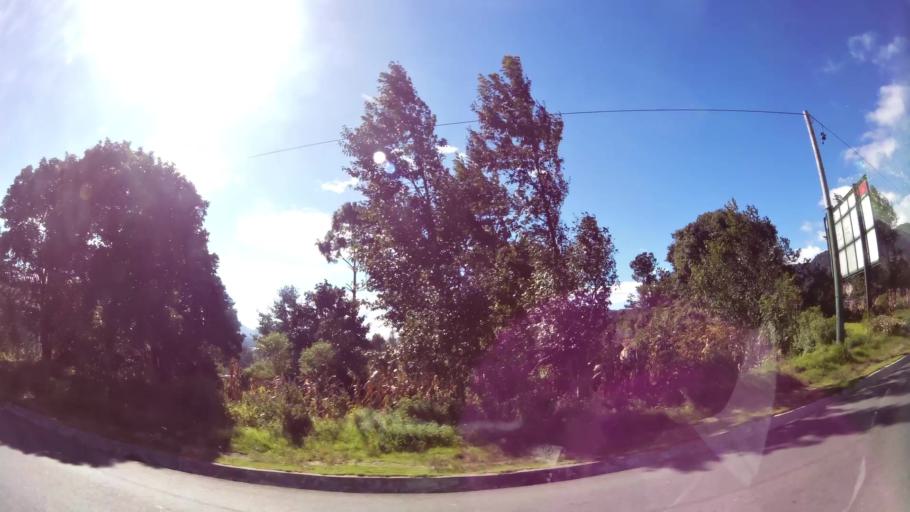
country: GT
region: Solola
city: Concepcion
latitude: 14.8217
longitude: -91.1785
